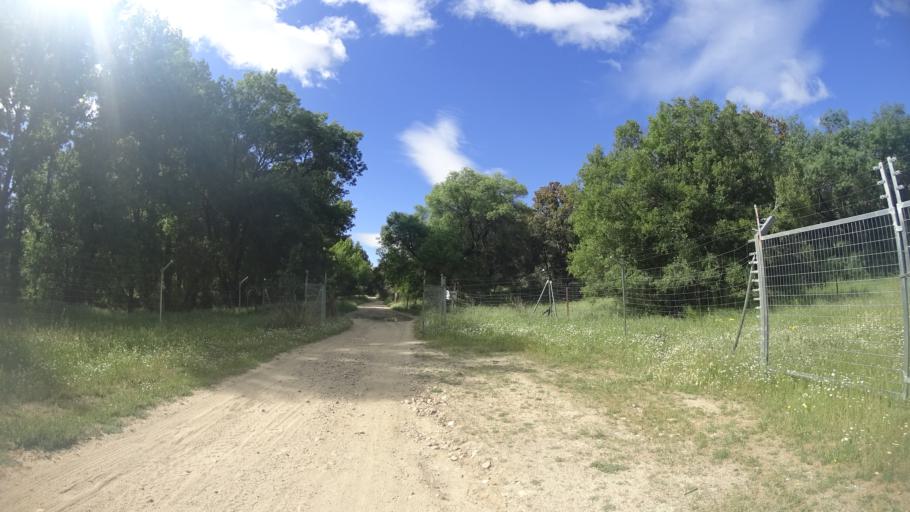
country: ES
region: Madrid
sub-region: Provincia de Madrid
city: Brunete
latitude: 40.4298
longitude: -3.9534
